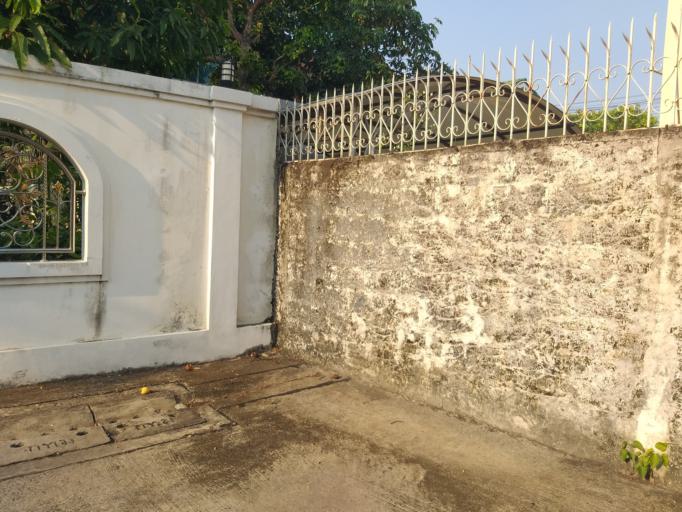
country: TH
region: Bangkok
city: Lat Phrao
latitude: 13.8216
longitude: 100.6139
